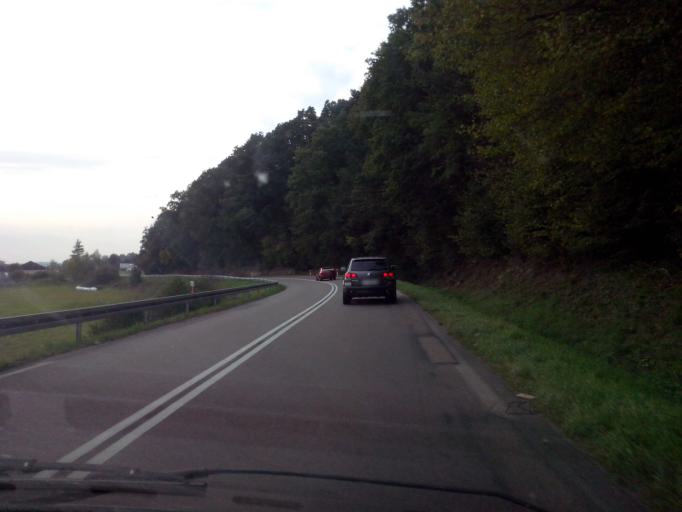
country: PL
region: Subcarpathian Voivodeship
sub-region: Powiat przeworski
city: Jawornik Polski
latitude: 49.8329
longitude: 22.2939
